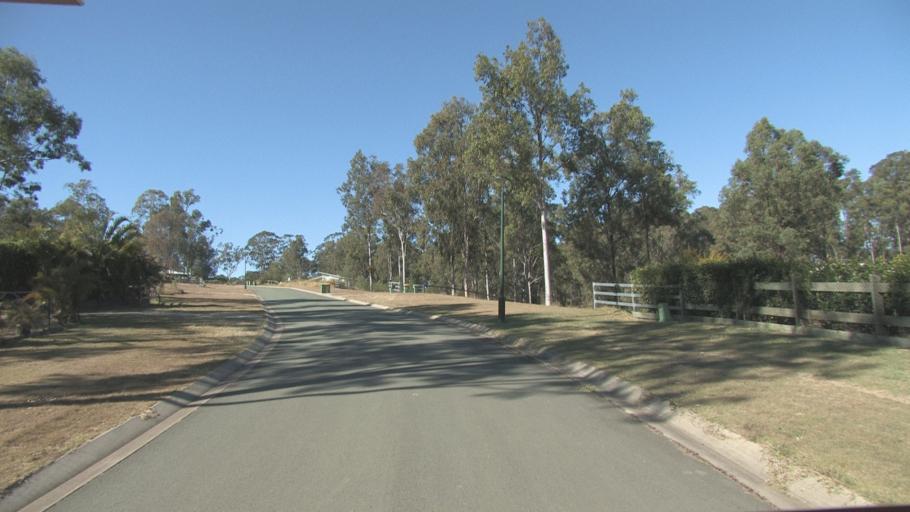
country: AU
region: Queensland
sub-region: Logan
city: Cedar Vale
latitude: -27.8929
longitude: 152.9934
